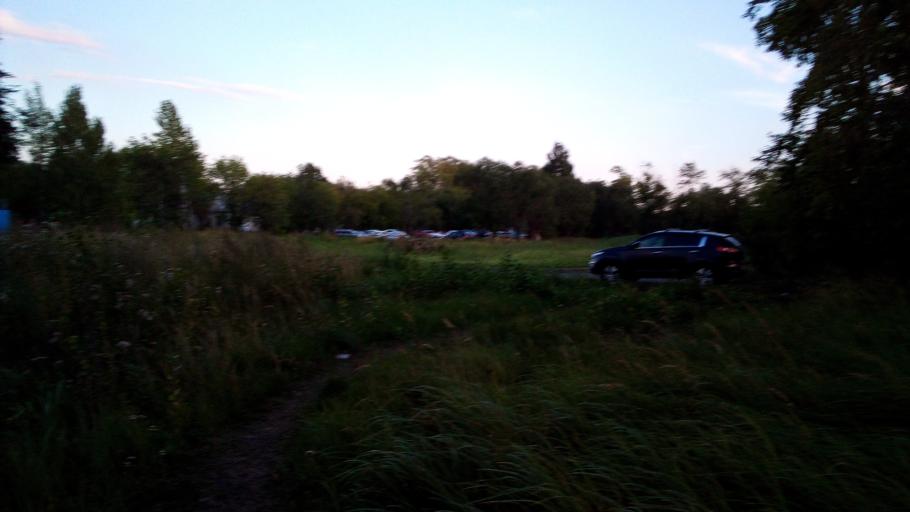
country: RU
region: Chelyabinsk
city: Potanino
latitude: 55.2924
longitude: 61.5117
